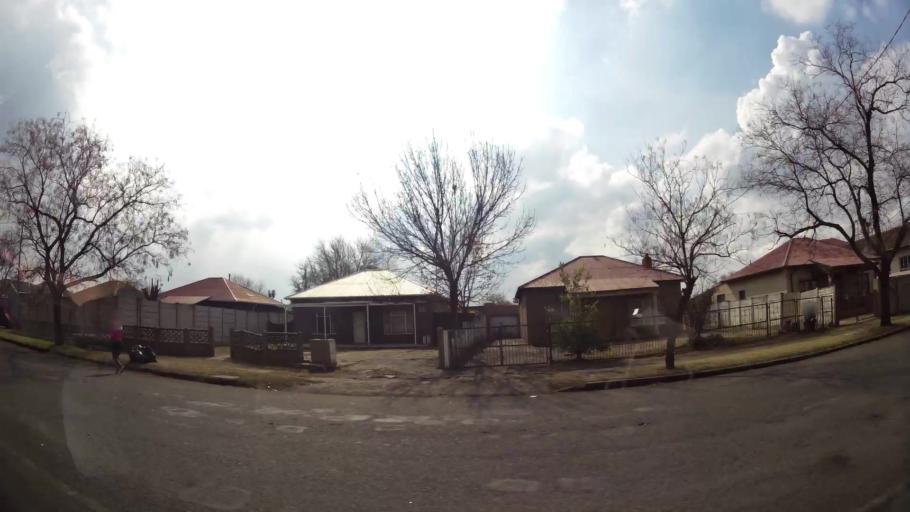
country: ZA
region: Gauteng
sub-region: Sedibeng District Municipality
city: Vereeniging
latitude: -26.6706
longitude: 27.9229
